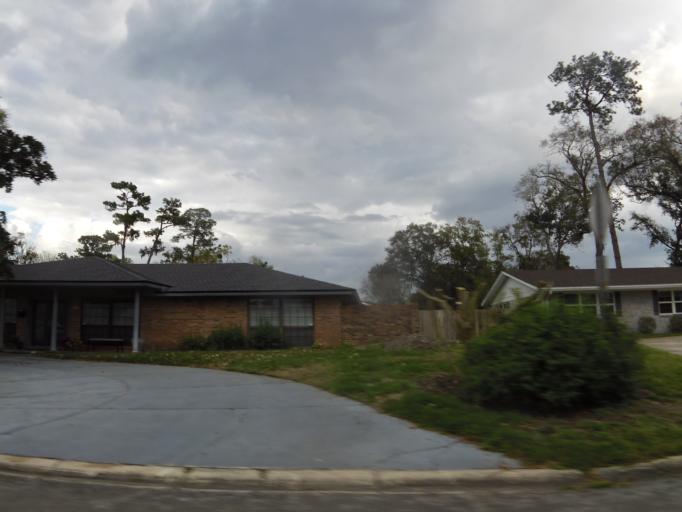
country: US
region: Florida
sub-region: Duval County
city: Jacksonville
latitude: 30.2529
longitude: -81.6373
